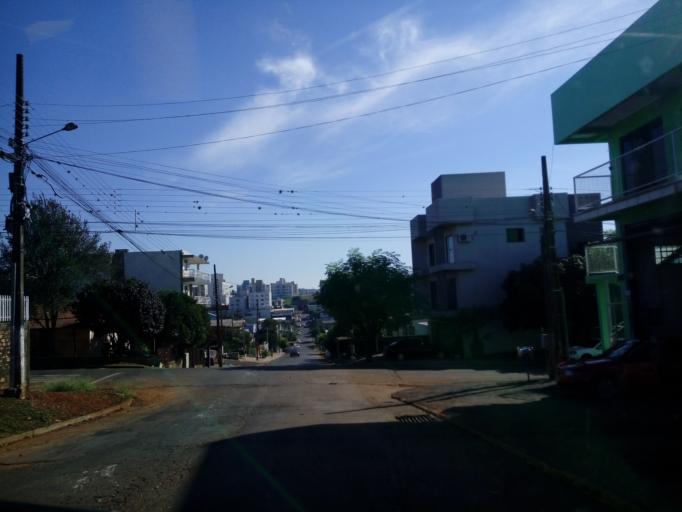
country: BR
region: Santa Catarina
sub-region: Chapeco
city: Chapeco
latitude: -27.0998
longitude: -52.6697
